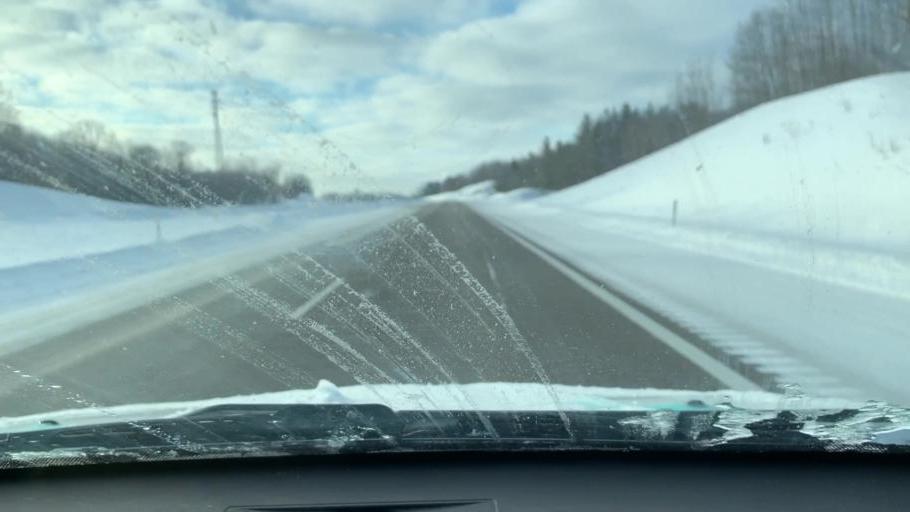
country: US
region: Michigan
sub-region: Wexford County
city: Manton
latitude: 44.3386
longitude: -85.4061
